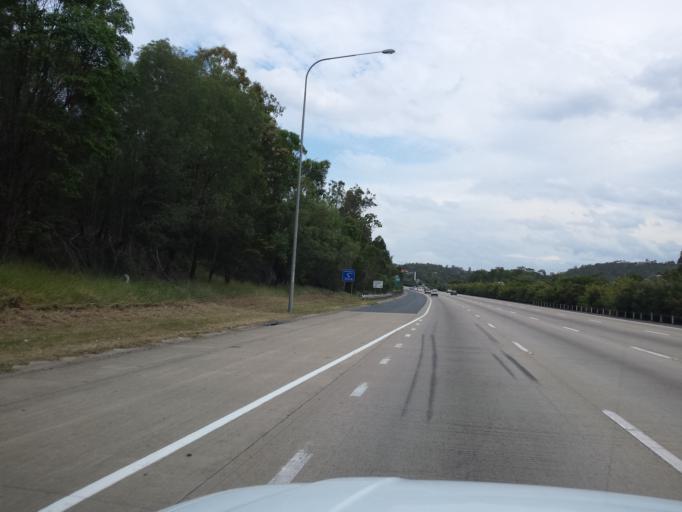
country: AU
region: Queensland
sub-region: Gold Coast
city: Upper Coomera
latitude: -27.9136
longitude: 153.3197
